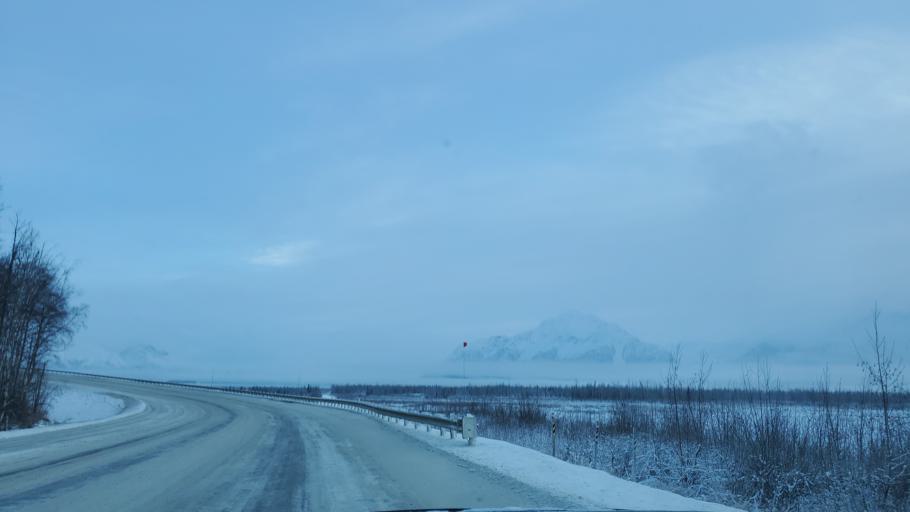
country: US
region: Alaska
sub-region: Matanuska-Susitna Borough
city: Gateway
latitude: 61.5500
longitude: -149.2849
